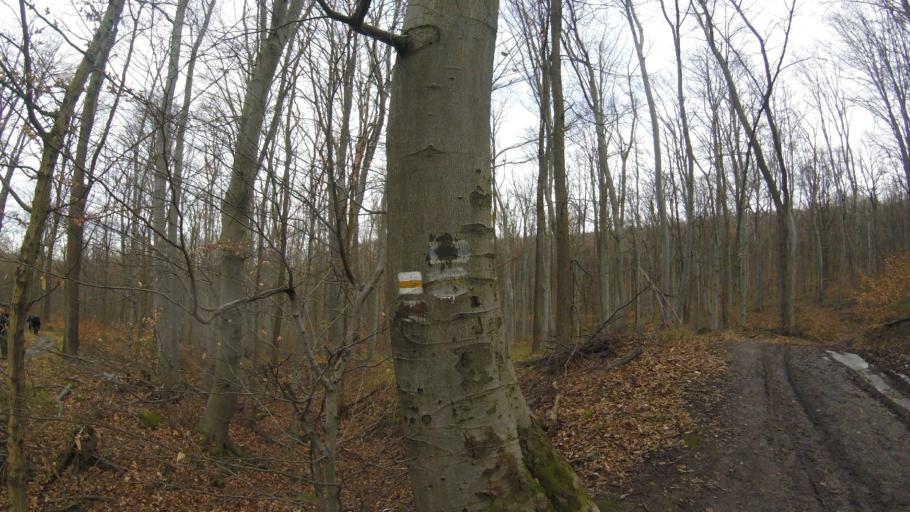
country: HU
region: Pest
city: Csobanka
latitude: 47.6935
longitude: 18.9744
